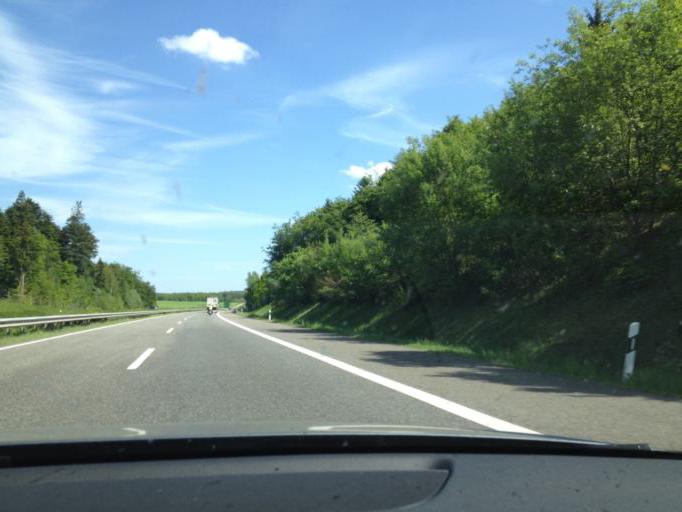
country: DE
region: Rheinland-Pfalz
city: Gindorf
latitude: 50.0195
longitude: 6.6576
